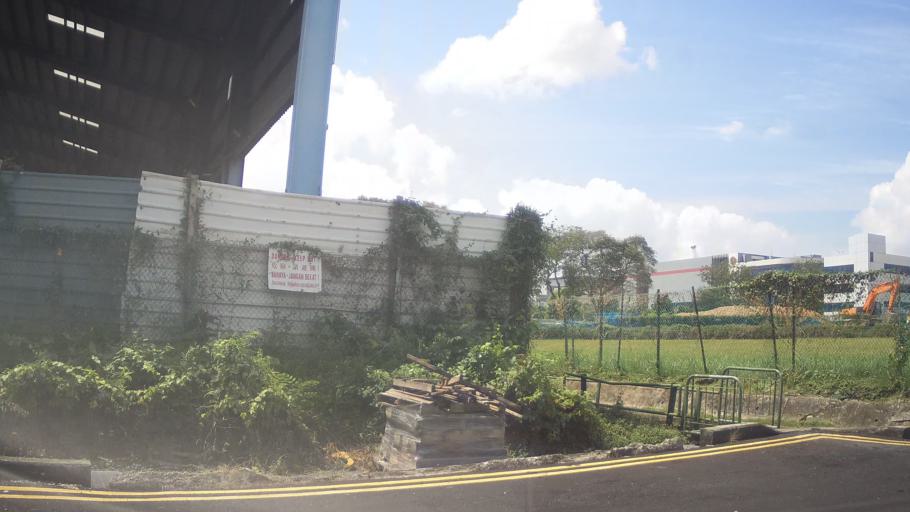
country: SG
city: Singapore
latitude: 1.3280
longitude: 103.7158
